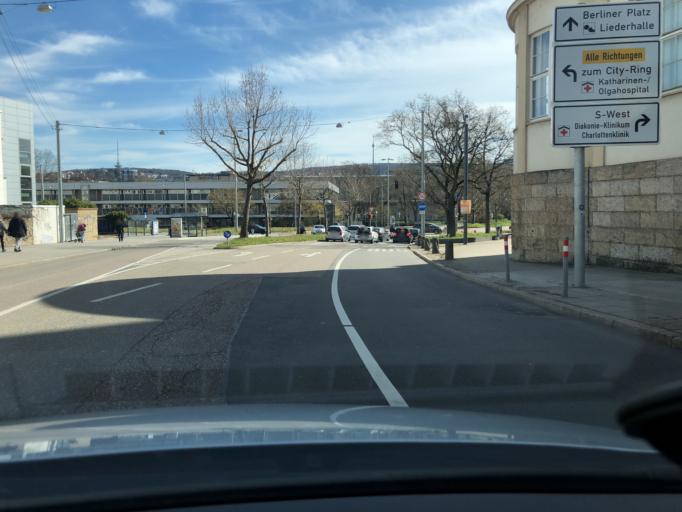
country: DE
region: Baden-Wuerttemberg
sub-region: Regierungsbezirk Stuttgart
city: Stuttgart
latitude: 48.7830
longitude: 9.1704
